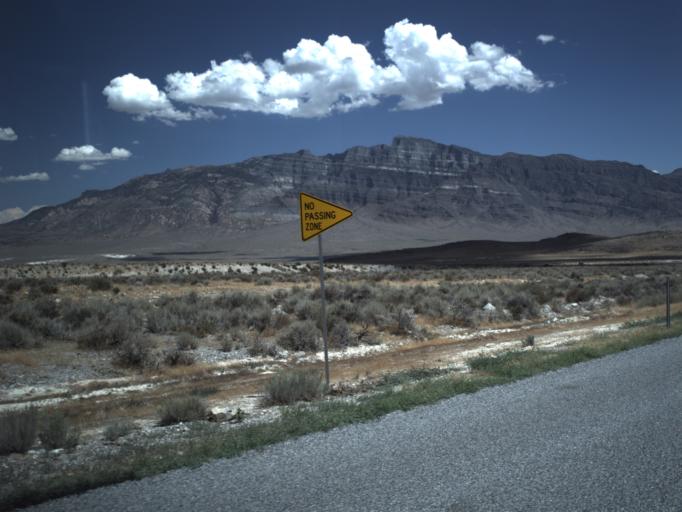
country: US
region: Utah
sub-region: Beaver County
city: Milford
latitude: 39.0875
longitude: -113.5461
